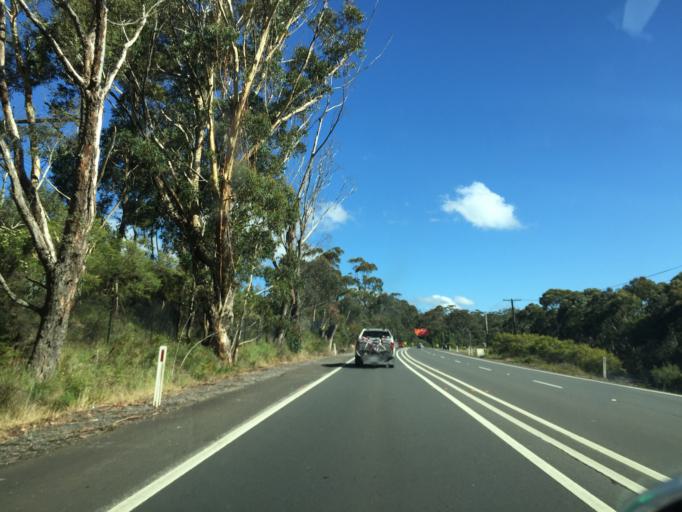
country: AU
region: New South Wales
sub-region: Blue Mountains Municipality
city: Katoomba
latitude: -33.6905
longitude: 150.2906
